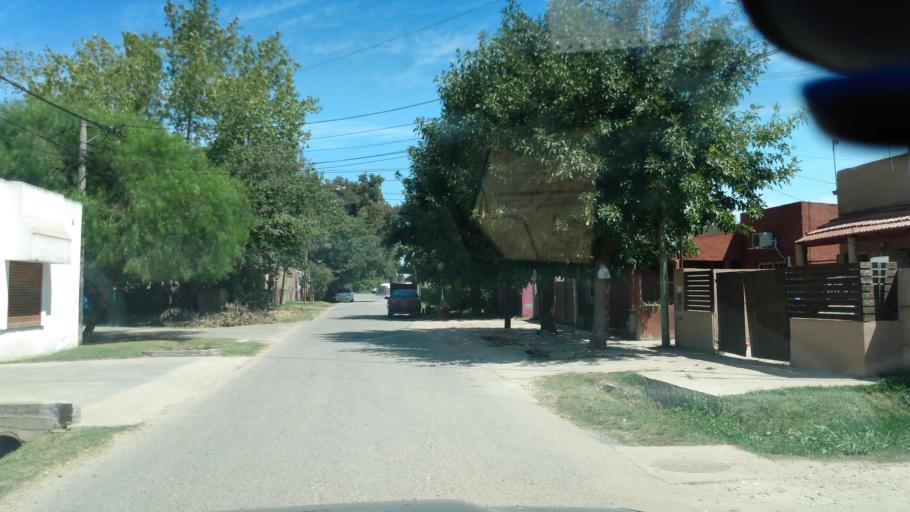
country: AR
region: Buenos Aires
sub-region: Partido de Lujan
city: Lujan
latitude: -34.5513
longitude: -59.1214
